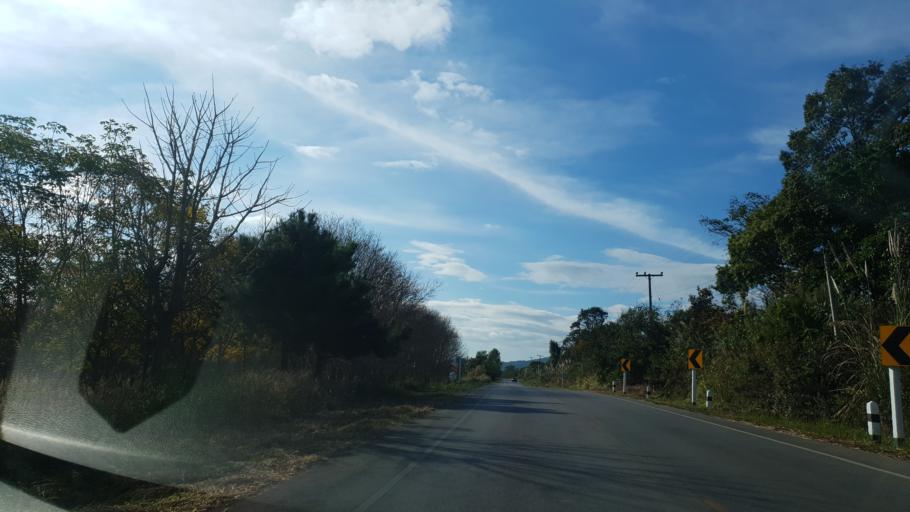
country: TH
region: Loei
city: Phu Ruea
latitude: 17.4456
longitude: 101.4982
